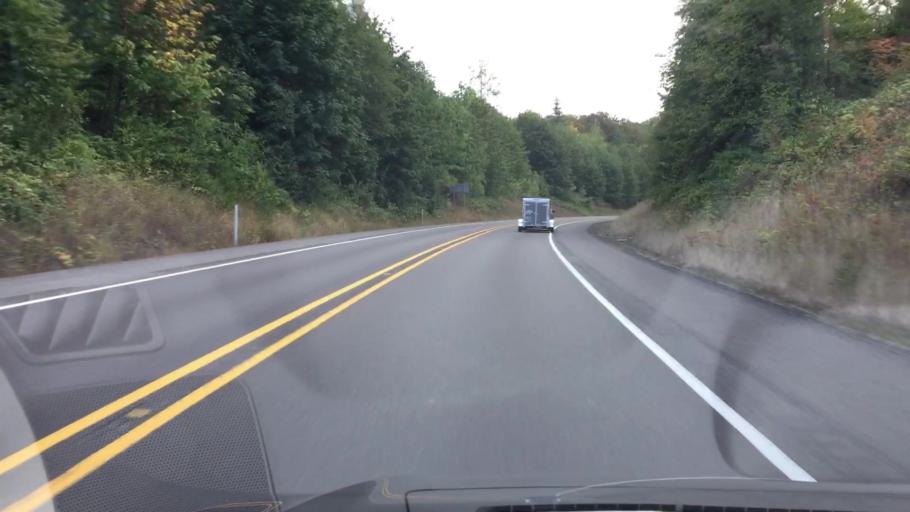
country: US
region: Washington
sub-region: Lewis County
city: Morton
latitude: 46.5201
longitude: -122.5580
